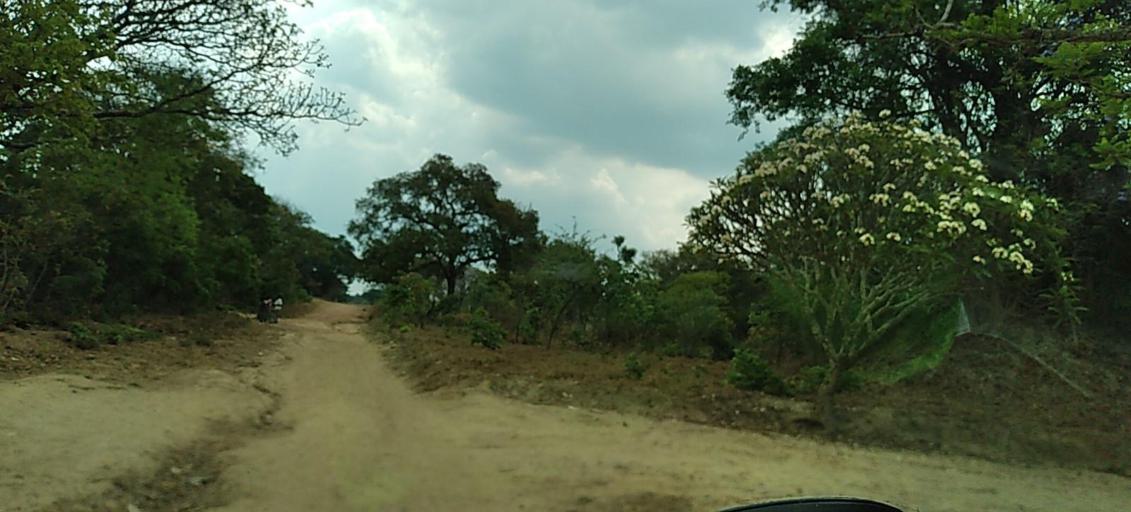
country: ZM
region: North-Western
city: Solwezi
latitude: -12.7867
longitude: 26.5190
